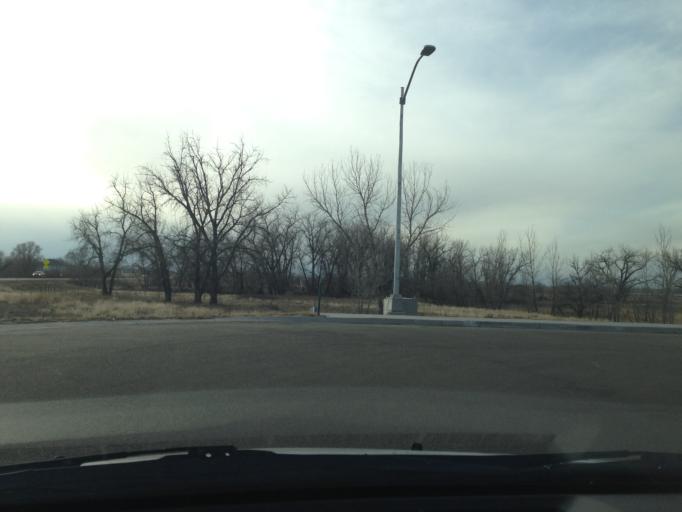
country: US
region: Colorado
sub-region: Weld County
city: Fort Lupton
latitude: 40.0803
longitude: -104.8253
